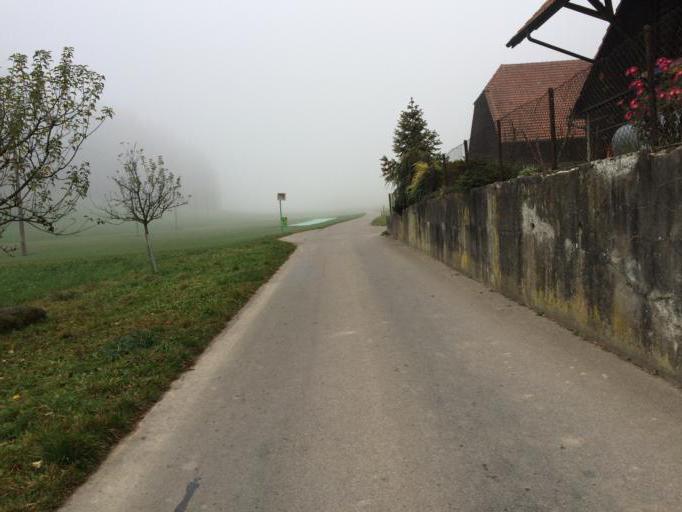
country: CH
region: Bern
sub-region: Bern-Mittelland District
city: Kehrsatz
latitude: 46.9075
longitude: 7.4574
